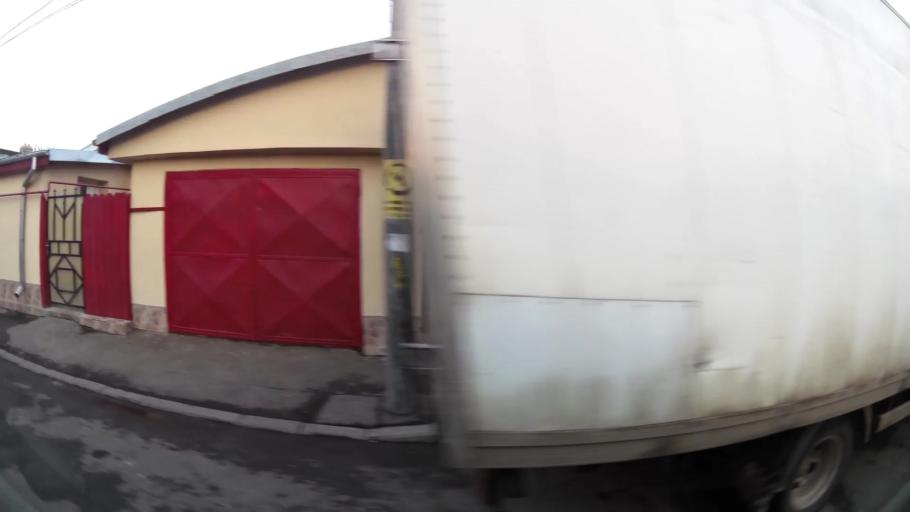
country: RO
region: Ilfov
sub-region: Voluntari City
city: Voluntari
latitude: 44.4763
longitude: 26.1727
